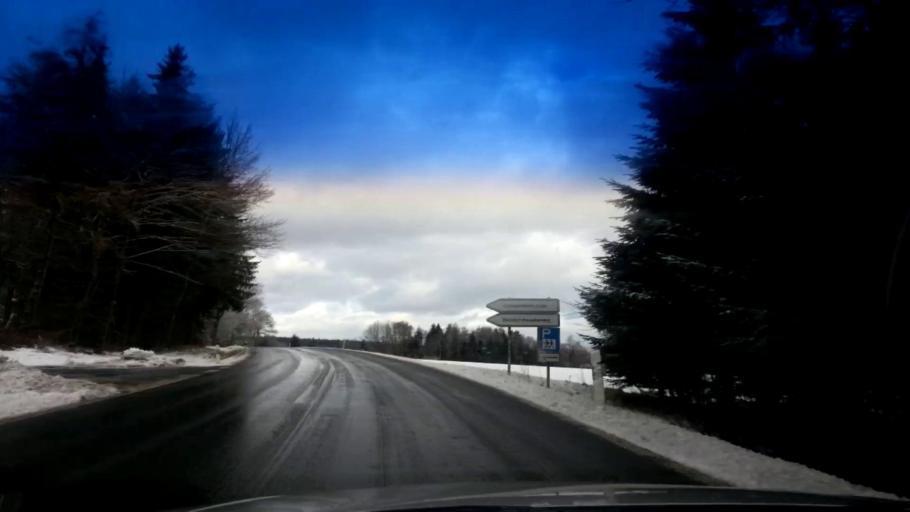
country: DE
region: Bavaria
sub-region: Upper Franconia
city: Kirchenlamitz
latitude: 50.1397
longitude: 11.9285
